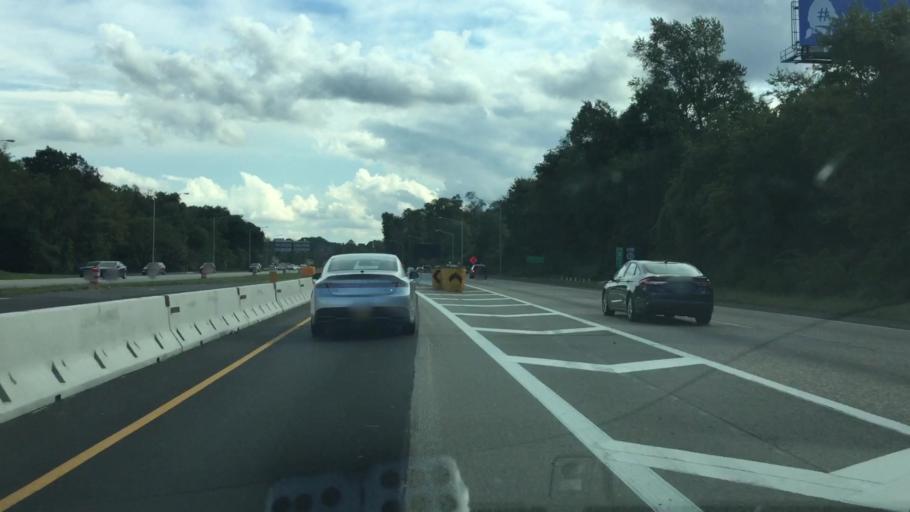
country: US
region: New Jersey
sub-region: Camden County
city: Glendora
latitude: 39.8302
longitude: -75.0883
